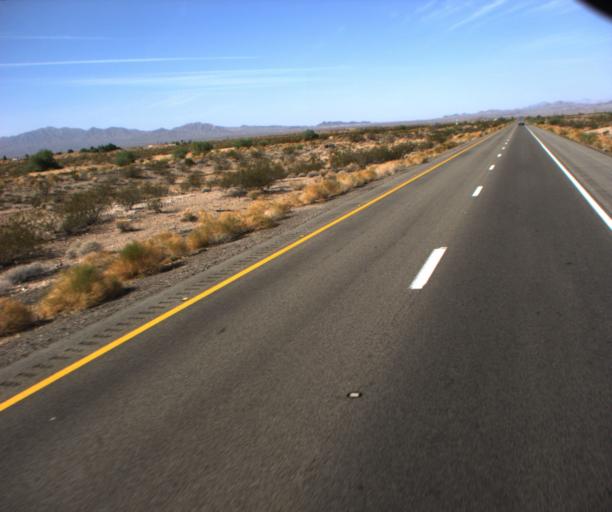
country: US
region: Arizona
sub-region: Mohave County
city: Desert Hills
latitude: 34.7628
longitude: -114.2059
